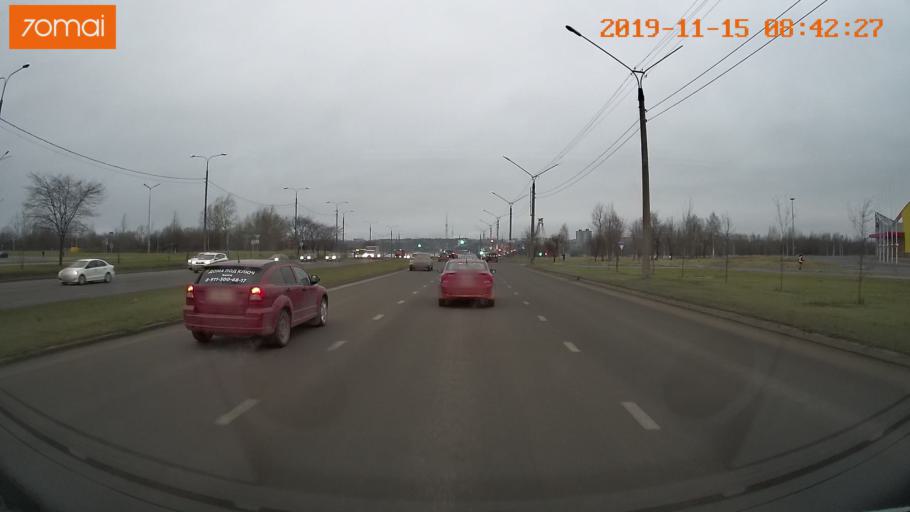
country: RU
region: Vologda
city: Cherepovets
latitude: 59.1030
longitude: 37.9077
